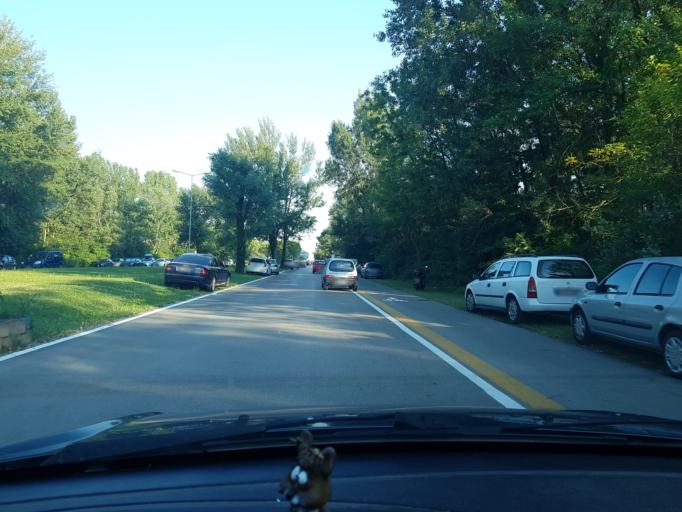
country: IT
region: Friuli Venezia Giulia
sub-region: Provincia di Gorizia
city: Monfalcone
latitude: 45.7786
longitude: 13.5249
